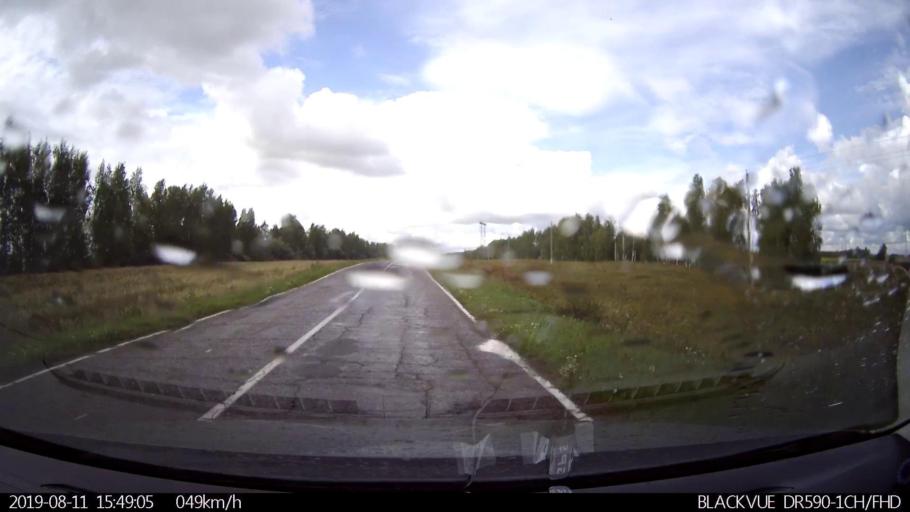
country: RU
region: Ulyanovsk
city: Ignatovka
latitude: 53.9017
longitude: 47.6547
